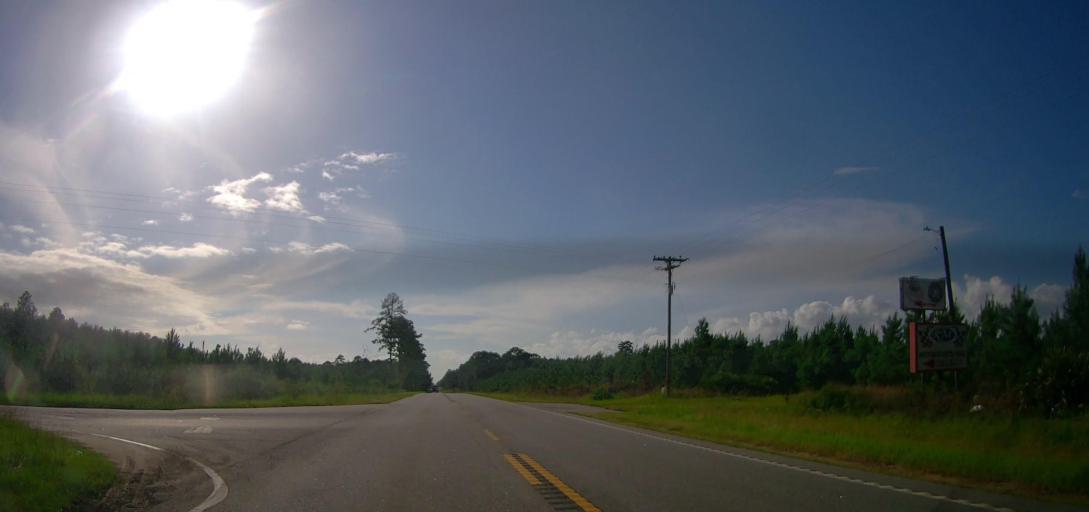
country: US
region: Georgia
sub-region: Coffee County
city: Douglas
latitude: 31.4577
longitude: -82.7410
